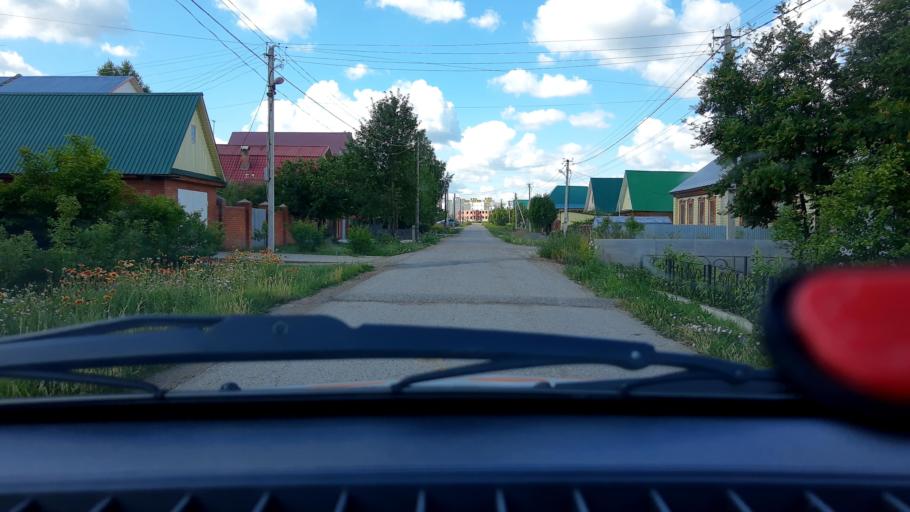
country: RU
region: Bashkortostan
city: Avdon
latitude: 54.4880
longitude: 55.8929
